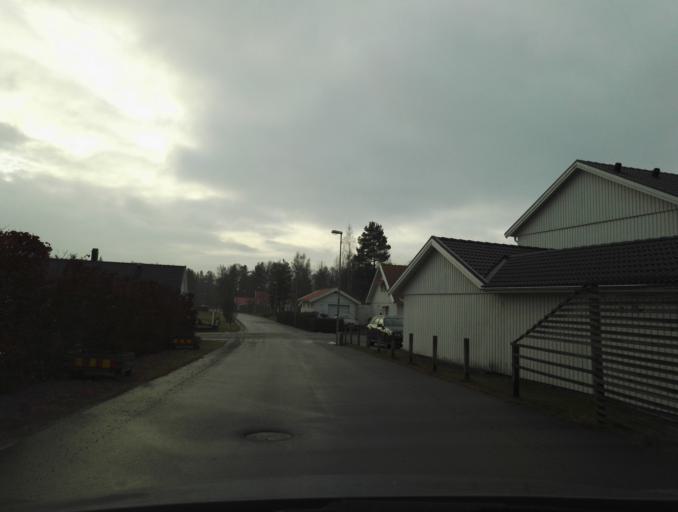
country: SE
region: Kronoberg
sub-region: Vaxjo Kommun
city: Vaexjoe
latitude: 56.9164
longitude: 14.7472
